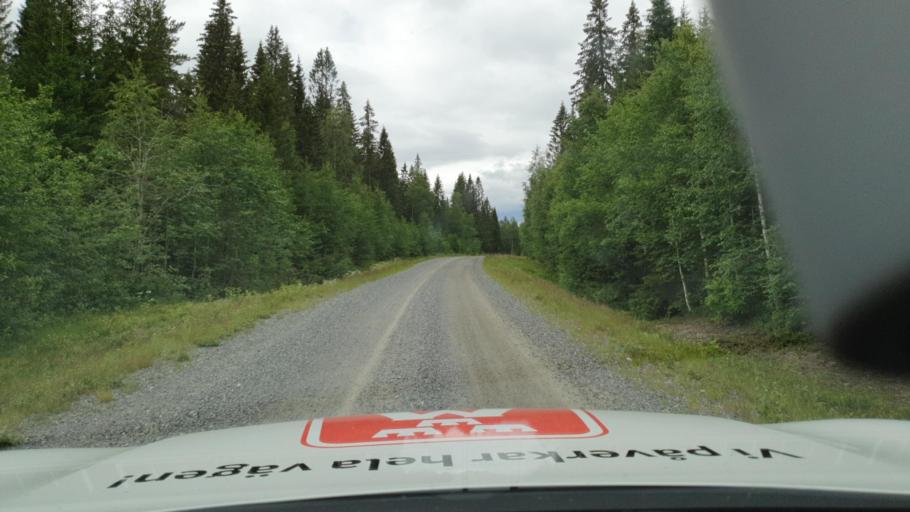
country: SE
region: Vaesterbotten
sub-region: Nordmalings Kommun
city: Nordmaling
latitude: 63.7388
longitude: 19.3931
